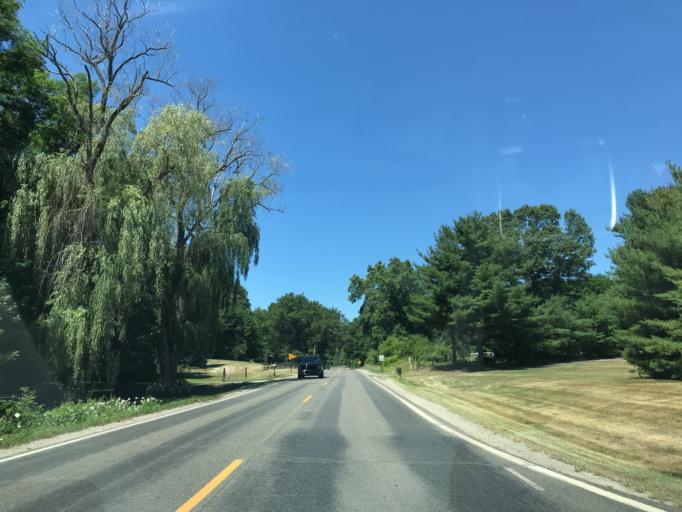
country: US
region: Michigan
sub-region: Livingston County
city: Whitmore Lake
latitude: 42.4686
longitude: -83.7374
